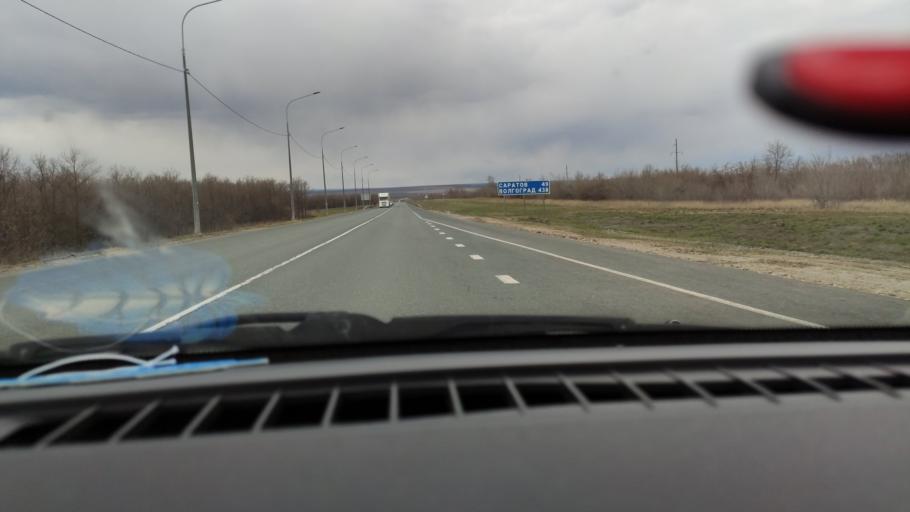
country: RU
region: Saratov
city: Yelshanka
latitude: 51.8264
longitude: 46.2804
